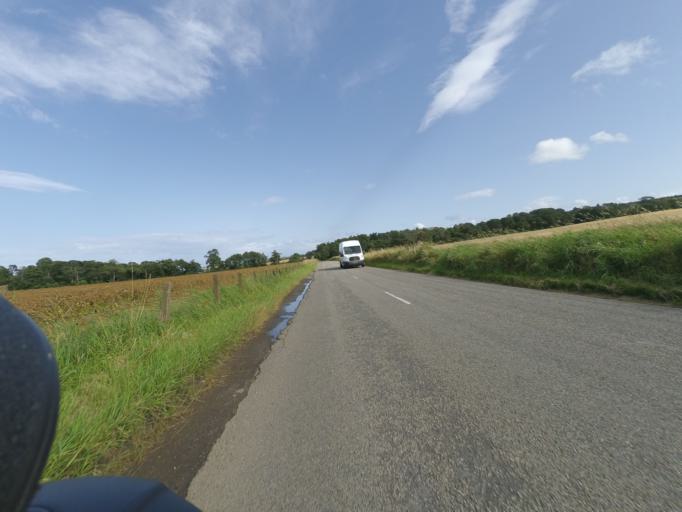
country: GB
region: Scotland
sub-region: Highland
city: Invergordon
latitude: 57.6561
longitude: -4.1729
